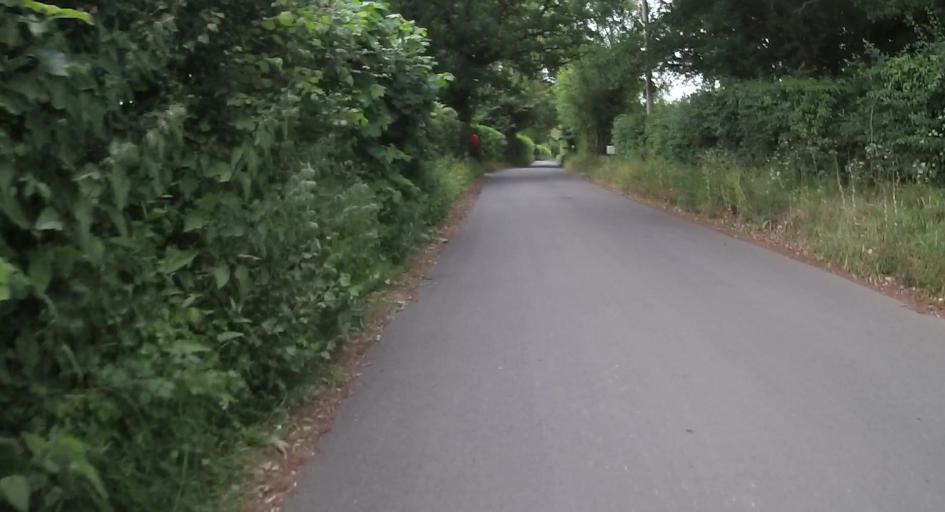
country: GB
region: England
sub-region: Surrey
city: Seale
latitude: 51.2119
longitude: -0.7364
